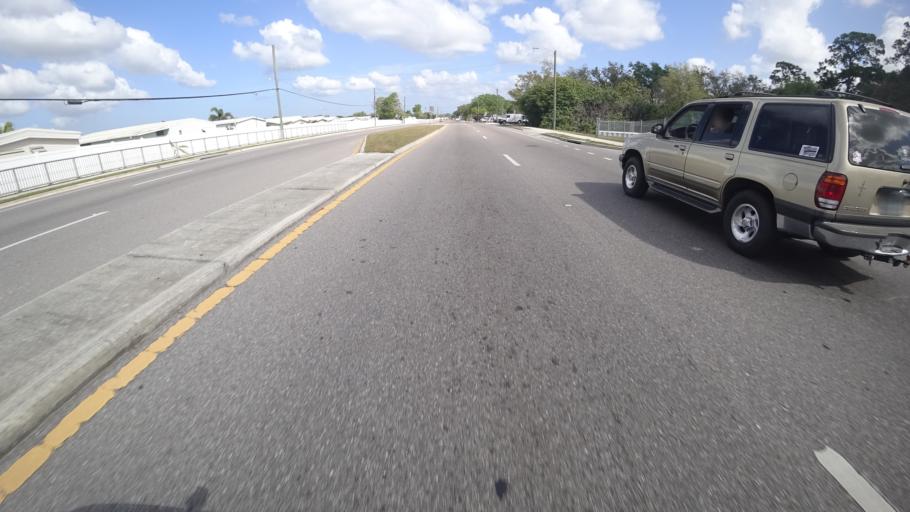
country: US
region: Florida
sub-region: Manatee County
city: West Samoset
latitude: 27.4424
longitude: -82.5548
